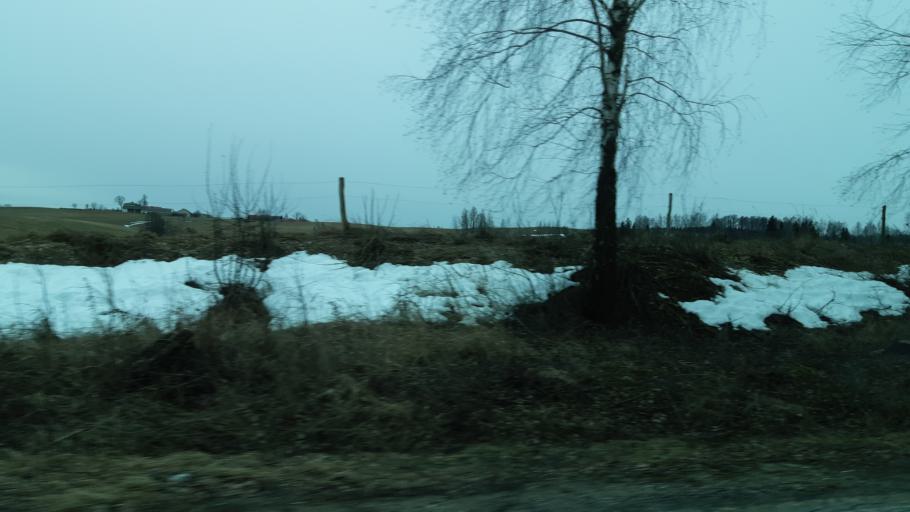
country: PL
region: Podlasie
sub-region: Suwalki
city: Suwalki
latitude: 54.3327
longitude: 22.9406
